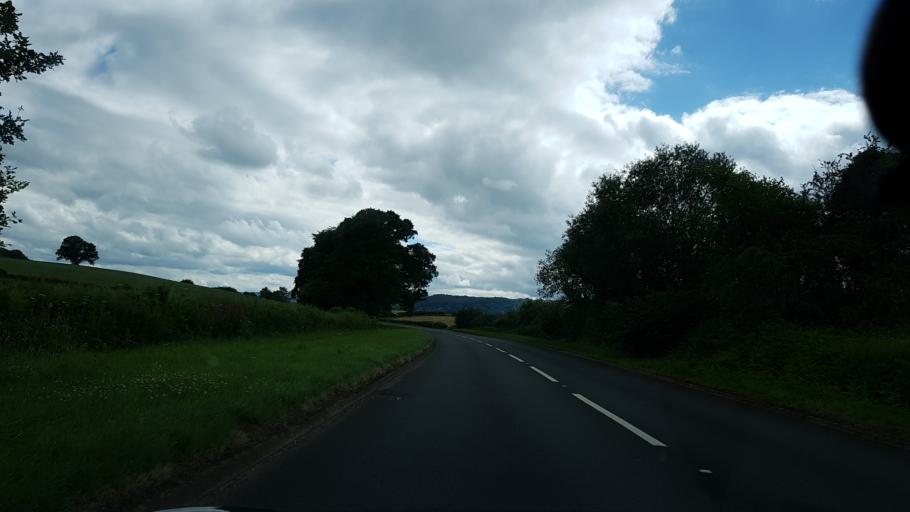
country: GB
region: Wales
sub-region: Monmouthshire
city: Abergavenny
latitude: 51.8724
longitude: -2.9879
